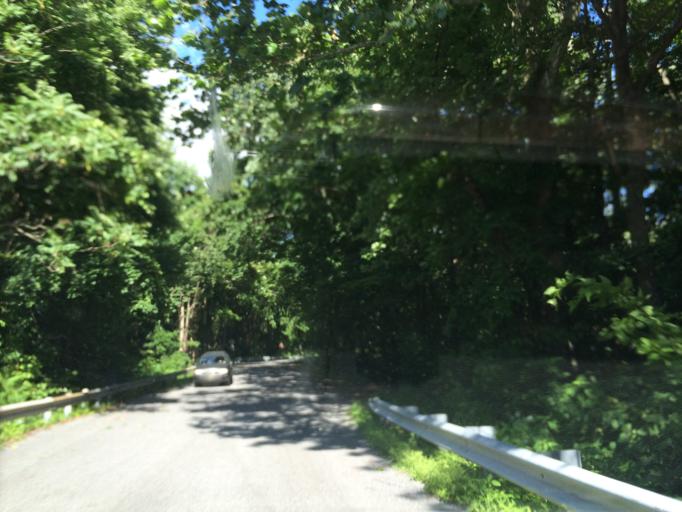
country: US
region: Maryland
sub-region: Washington County
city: Smithsburg
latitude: 39.6661
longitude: -77.5499
